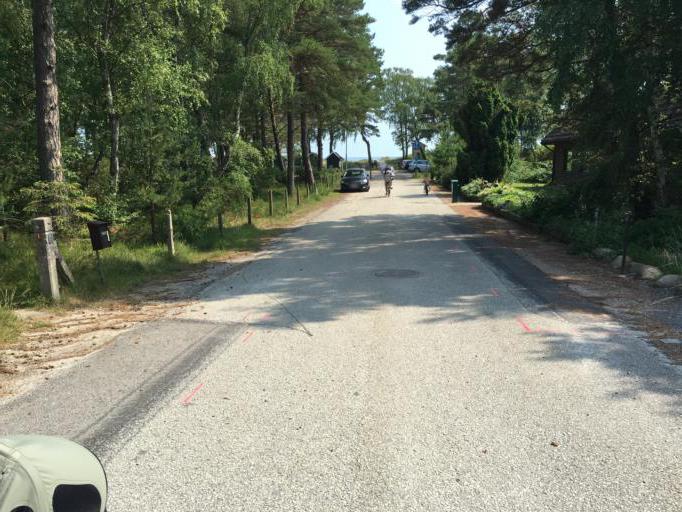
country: SE
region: Skane
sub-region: Vellinge Kommun
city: Hollviken
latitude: 55.4013
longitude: 12.9510
